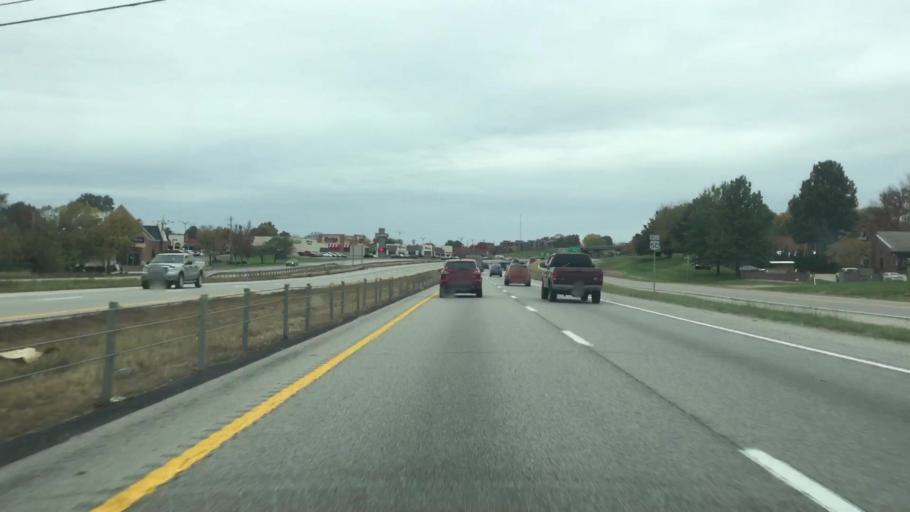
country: US
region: Missouri
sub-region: Jackson County
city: Lees Summit
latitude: 38.9148
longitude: -94.3980
